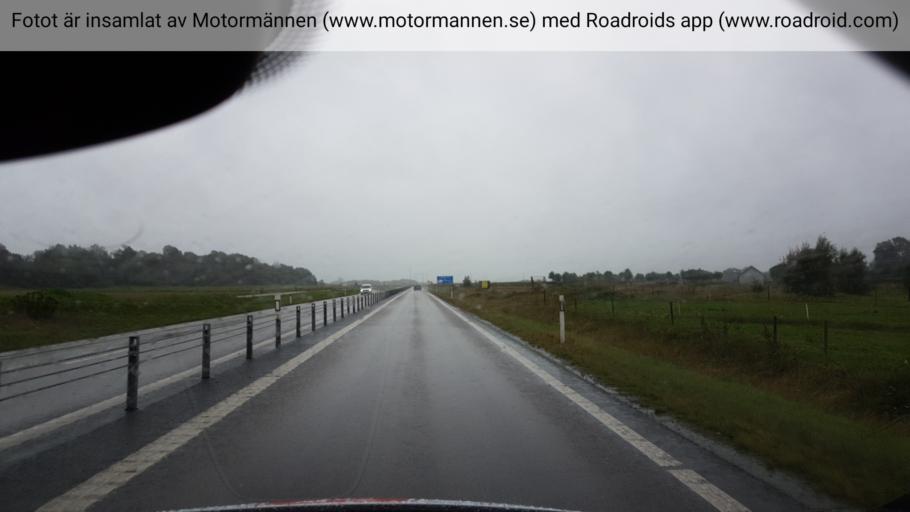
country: SE
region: Halland
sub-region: Laholms Kommun
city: Veinge
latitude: 56.5599
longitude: 13.0329
